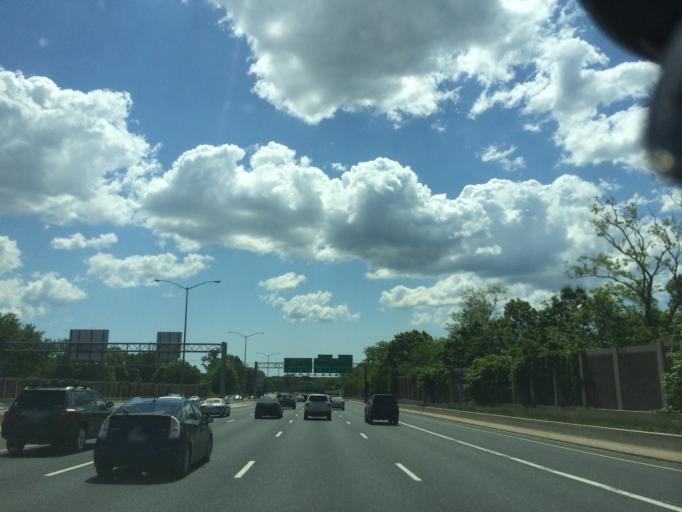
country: US
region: Maryland
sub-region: Baltimore County
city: Charlestown
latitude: 39.2608
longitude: -76.7042
